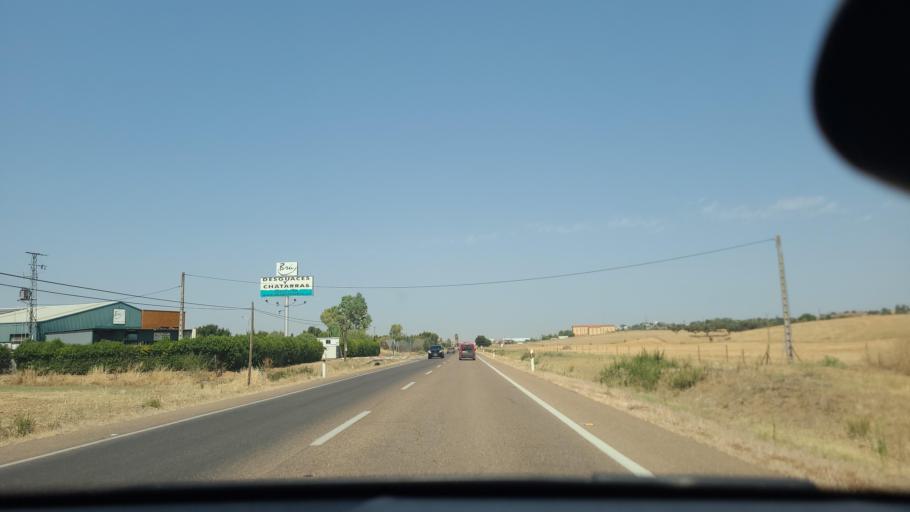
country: ES
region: Extremadura
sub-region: Provincia de Badajoz
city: Badajoz
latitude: 38.8438
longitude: -6.9326
